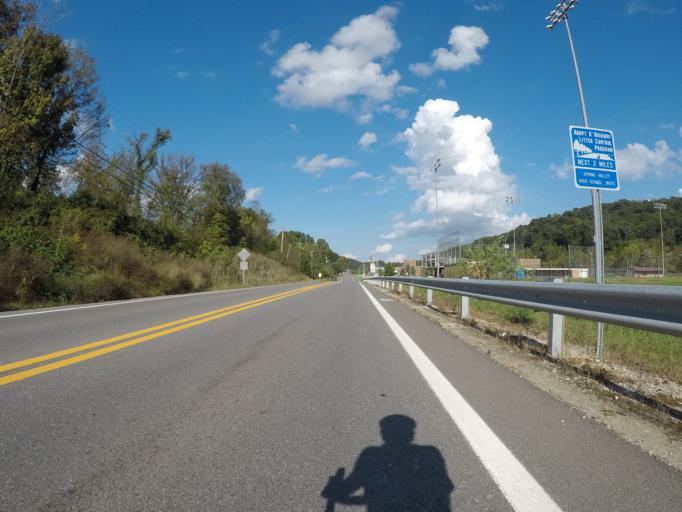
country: US
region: Ohio
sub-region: Lawrence County
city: Burlington
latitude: 38.3772
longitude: -82.5307
